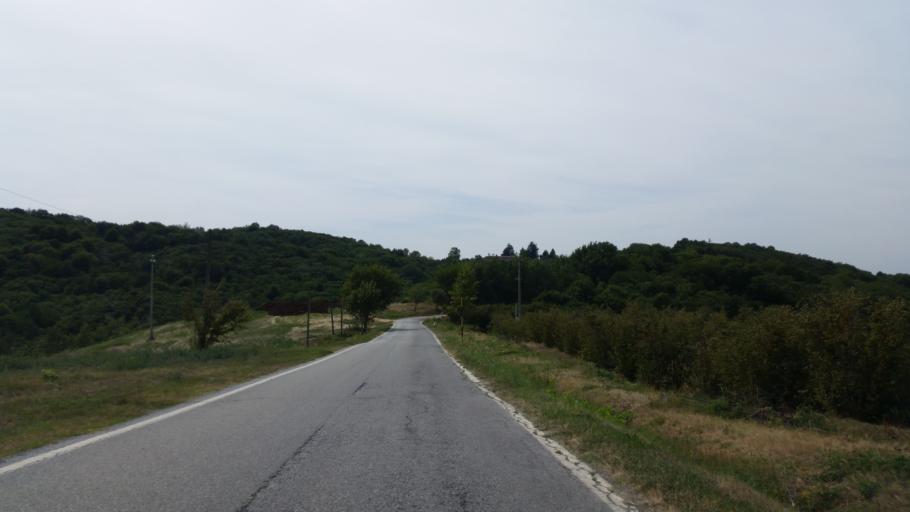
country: IT
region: Piedmont
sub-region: Provincia di Cuneo
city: Benevello
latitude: 44.6523
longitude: 8.1269
